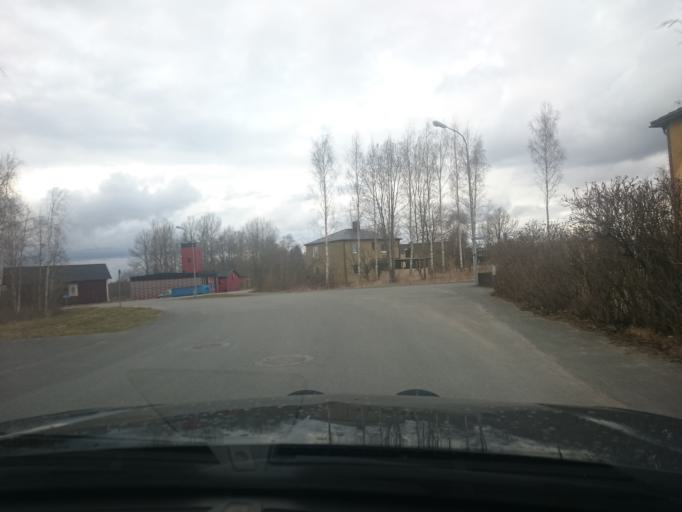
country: SE
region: Joenkoeping
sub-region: Vetlanda Kommun
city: Vetlanda
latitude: 57.2991
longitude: 15.1248
